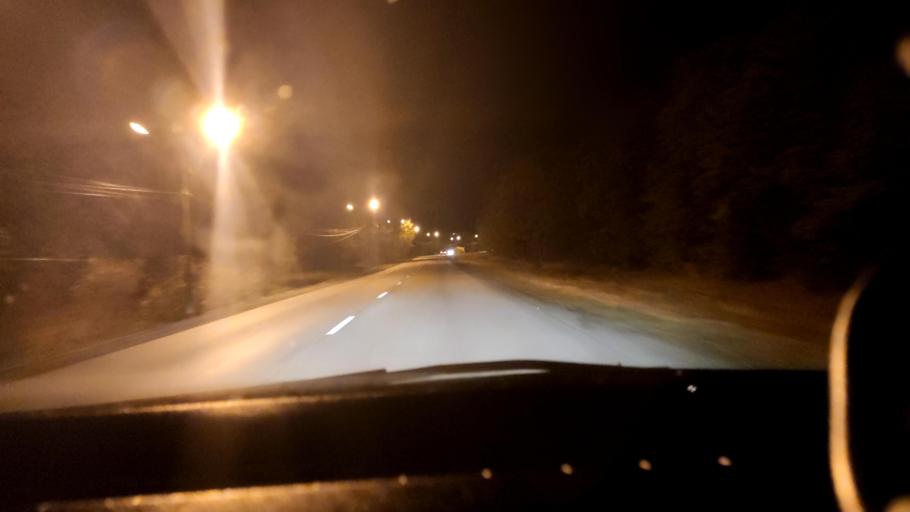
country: RU
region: Voronezj
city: Shilovo
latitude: 51.5570
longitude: 39.1033
